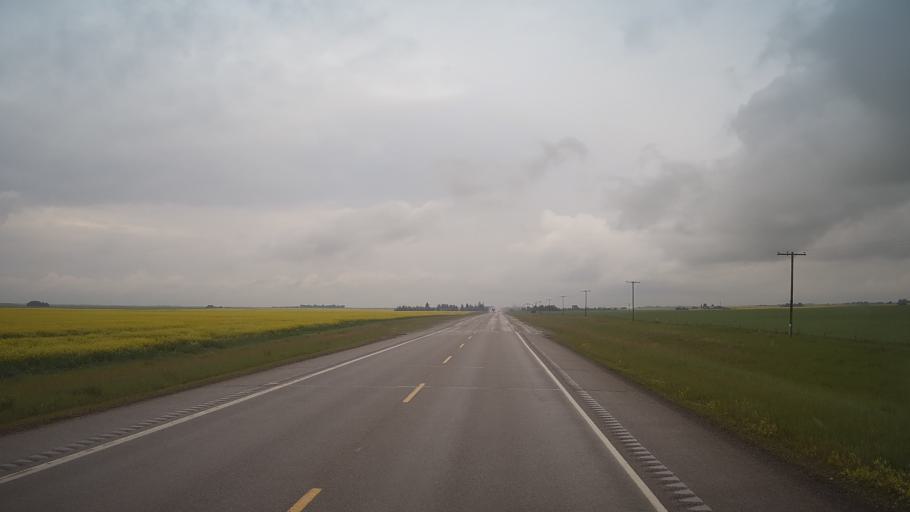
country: CA
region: Saskatchewan
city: Unity
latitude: 52.4349
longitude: -109.0138
